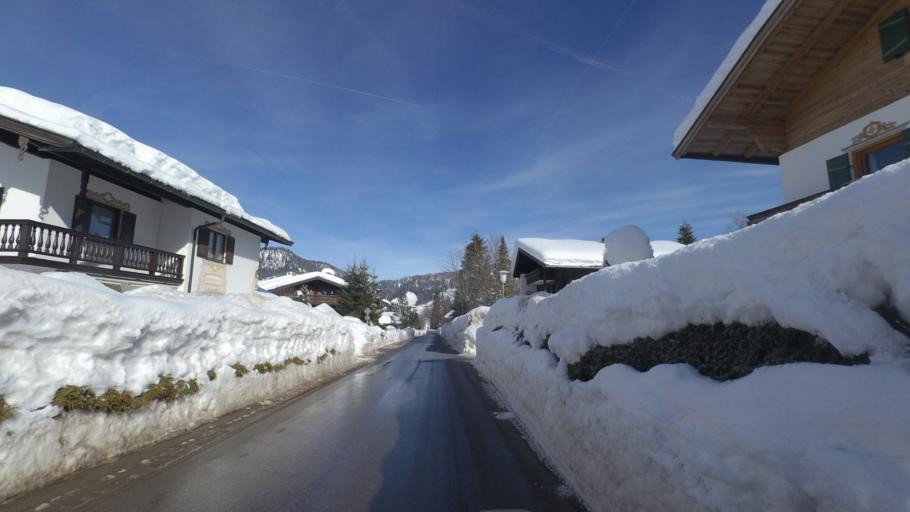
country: DE
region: Bavaria
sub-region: Upper Bavaria
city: Reit im Winkl
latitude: 47.6630
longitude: 12.4764
